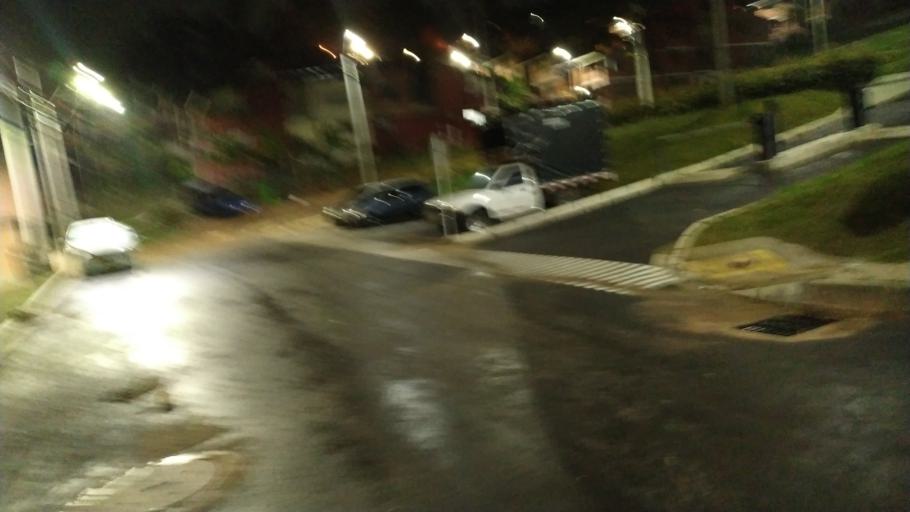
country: CO
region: Antioquia
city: Rionegro
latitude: 6.1595
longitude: -75.3790
